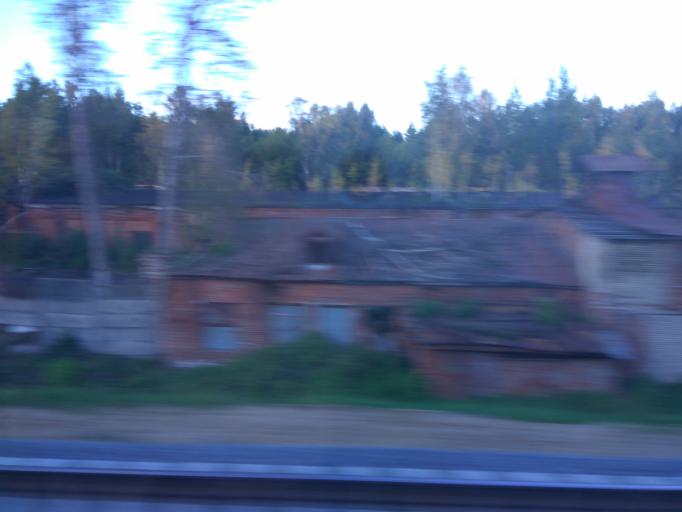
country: RU
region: Moscow
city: Rostokino
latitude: 55.8342
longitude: 37.6889
